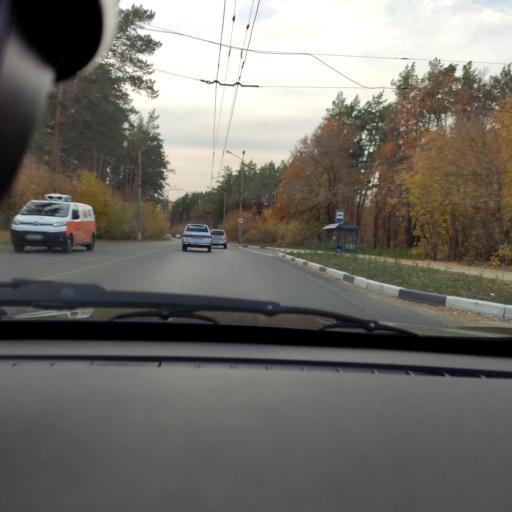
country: RU
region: Samara
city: Tol'yatti
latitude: 53.4782
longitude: 49.3580
